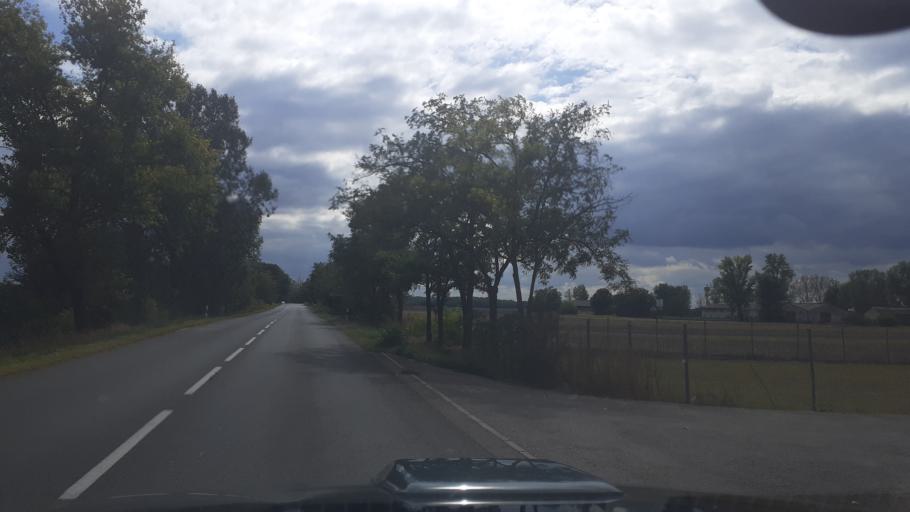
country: HU
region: Bacs-Kiskun
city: Apostag
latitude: 46.8831
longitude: 18.9774
